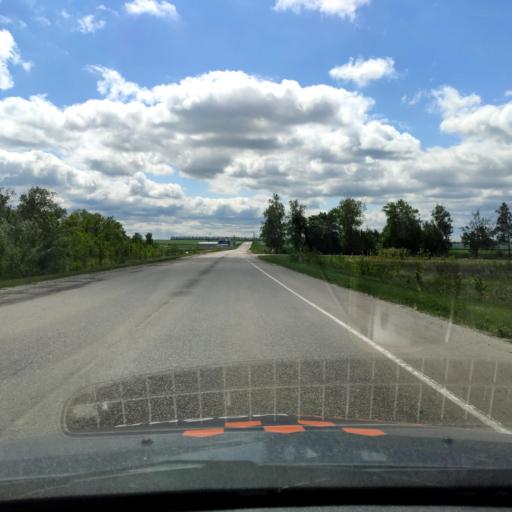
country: RU
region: Voronezj
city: Novaya Usman'
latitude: 51.6088
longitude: 39.3377
